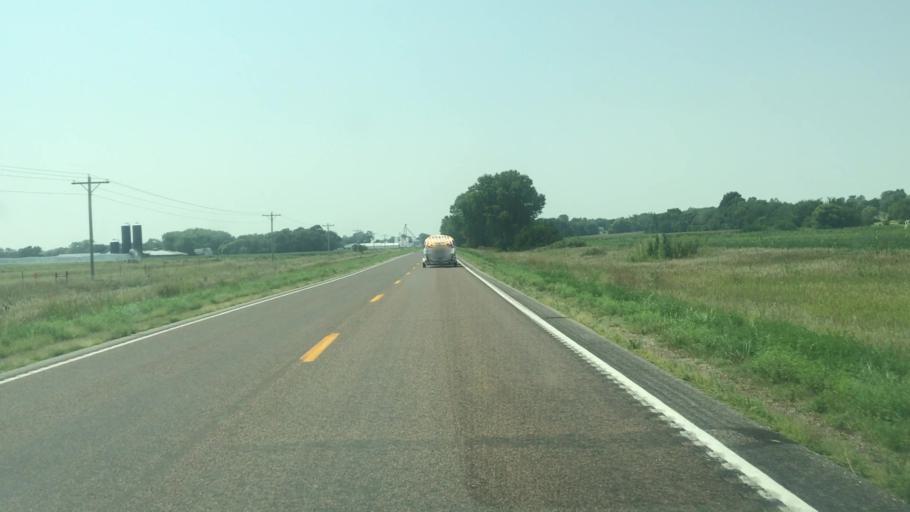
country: US
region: Nebraska
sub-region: Buffalo County
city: Ravenna
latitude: 41.0764
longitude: -98.7020
